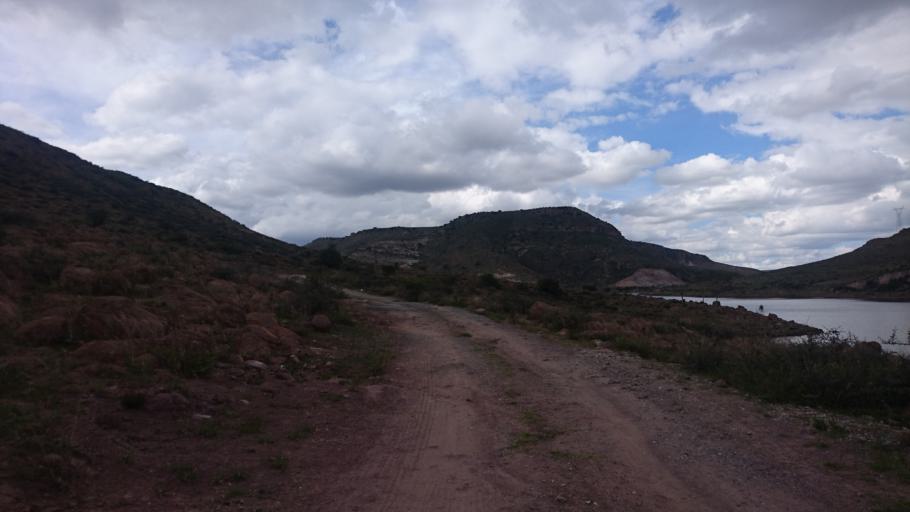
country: MX
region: San Luis Potosi
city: Escalerillas
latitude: 22.0832
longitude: -101.1010
